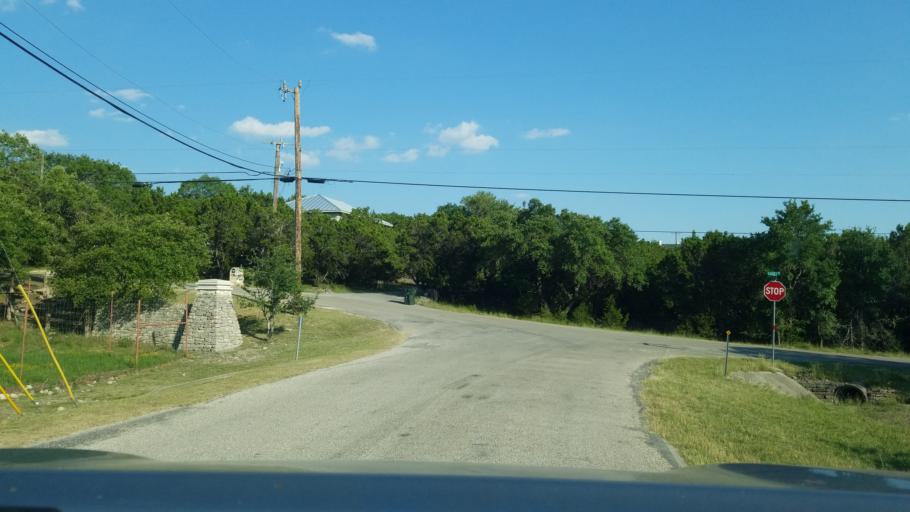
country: US
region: Texas
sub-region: Comal County
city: Bulverde
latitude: 29.7757
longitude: -98.4420
